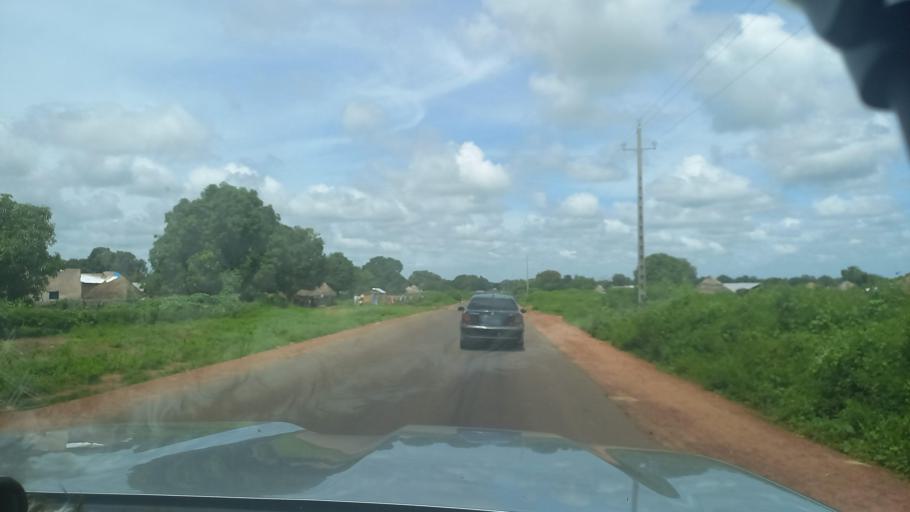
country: GM
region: Lower River
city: Kaiaf
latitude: 13.1979
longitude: -15.5527
